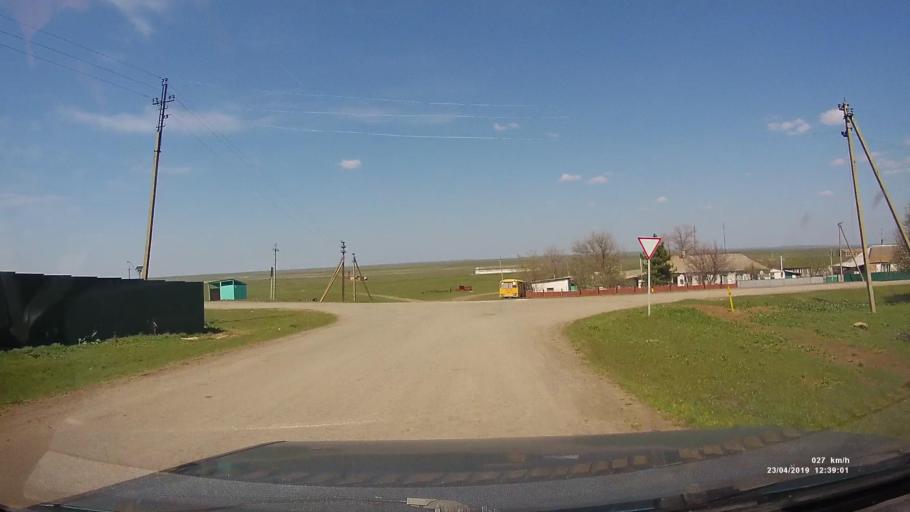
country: RU
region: Kalmykiya
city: Yashalta
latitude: 46.4336
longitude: 42.7113
